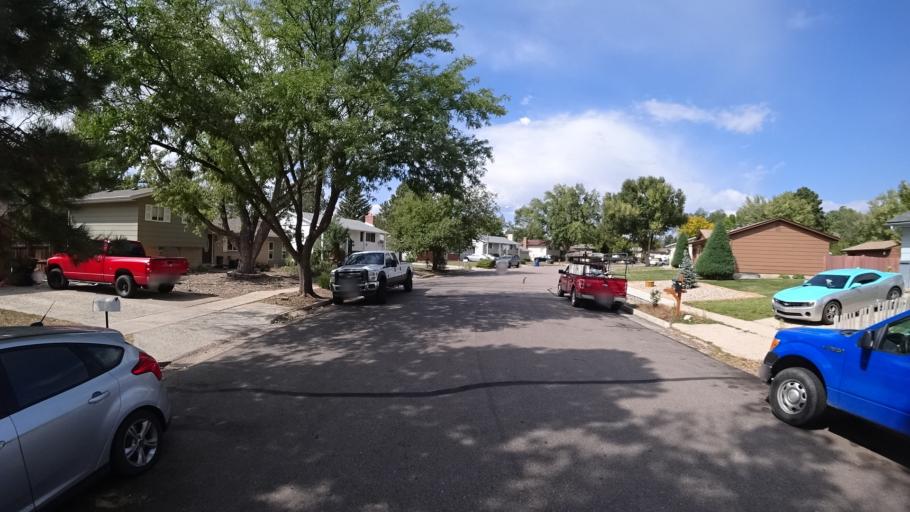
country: US
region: Colorado
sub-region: El Paso County
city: Cimarron Hills
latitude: 38.8510
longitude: -104.7406
